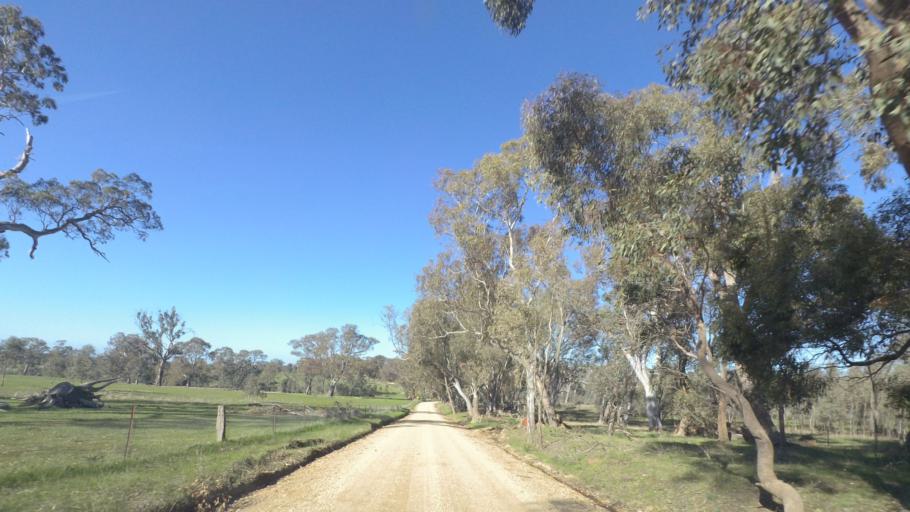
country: AU
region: Victoria
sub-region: Mount Alexander
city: Castlemaine
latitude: -36.9659
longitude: 144.3445
